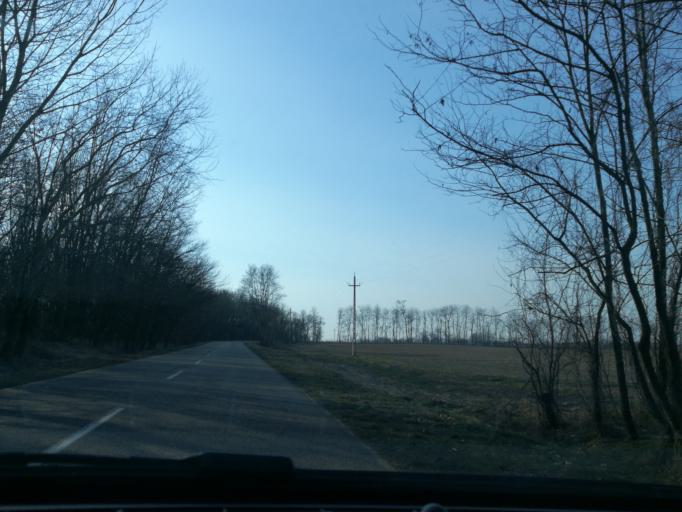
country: HU
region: Szabolcs-Szatmar-Bereg
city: Levelek
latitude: 47.9921
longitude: 21.9679
